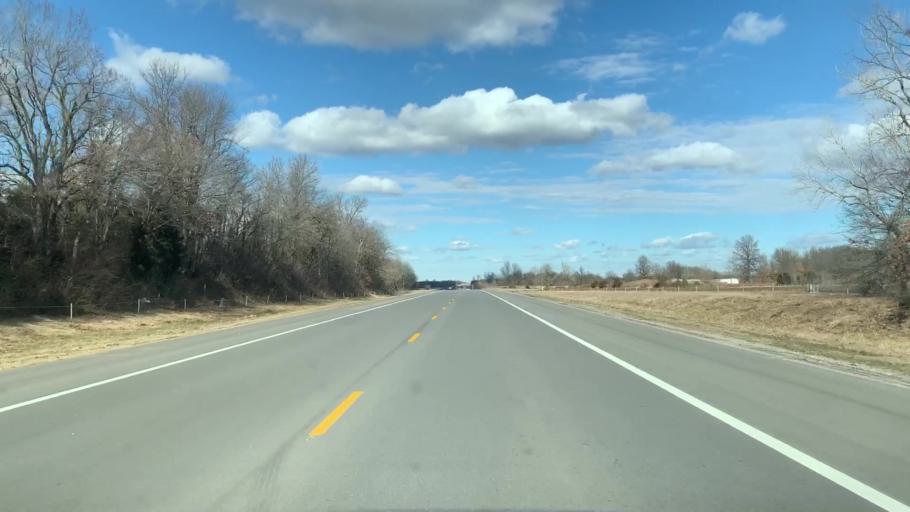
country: US
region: Kansas
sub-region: Cherokee County
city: Columbus
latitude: 37.2572
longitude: -94.8319
